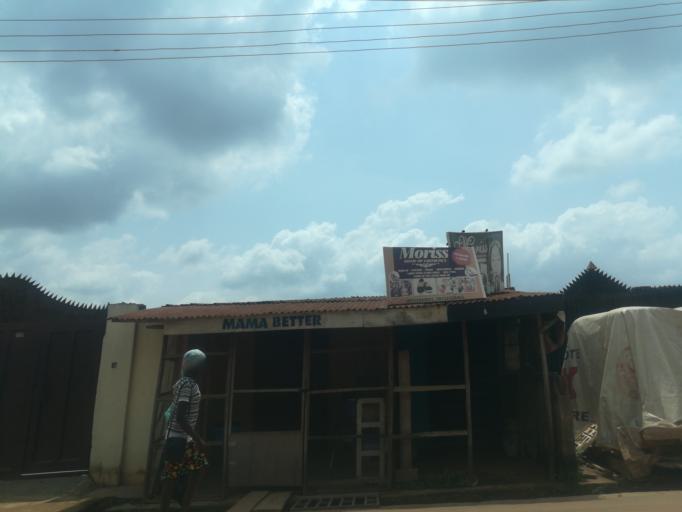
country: NG
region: Oyo
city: Ibadan
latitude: 7.4487
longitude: 3.9528
